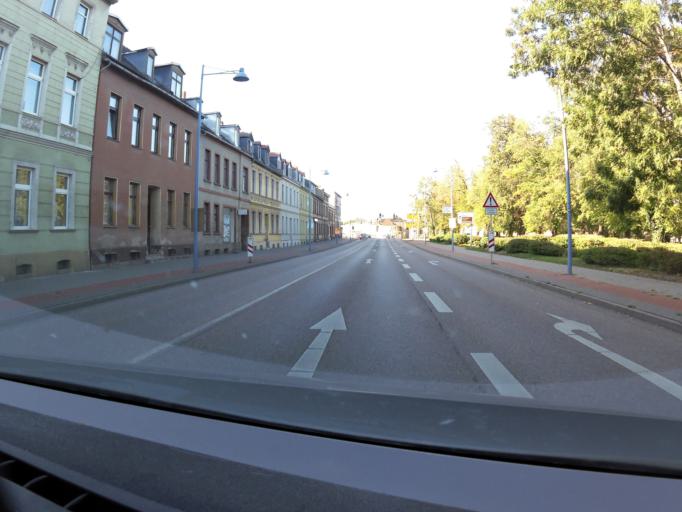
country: DE
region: Saxony-Anhalt
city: Bernburg
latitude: 51.7965
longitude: 11.7499
